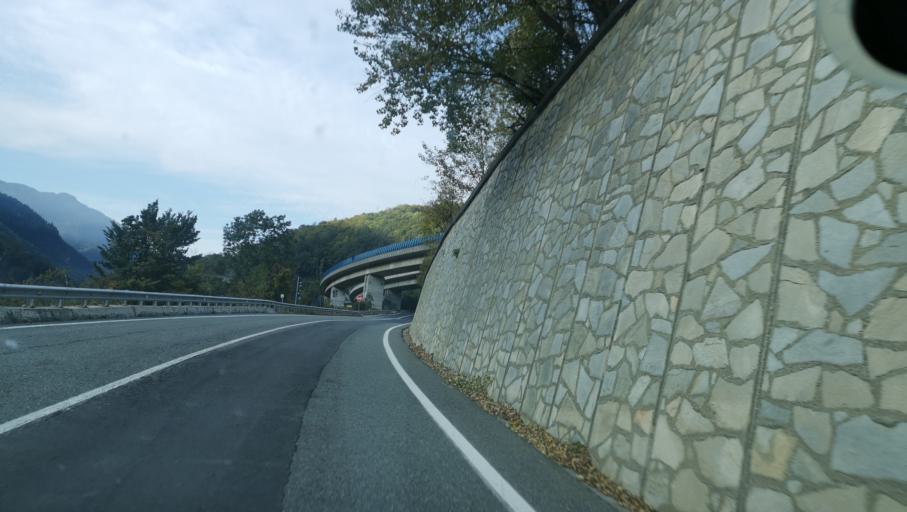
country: IT
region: Piedmont
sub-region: Provincia di Torino
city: Exilles
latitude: 45.0909
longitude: 6.9156
